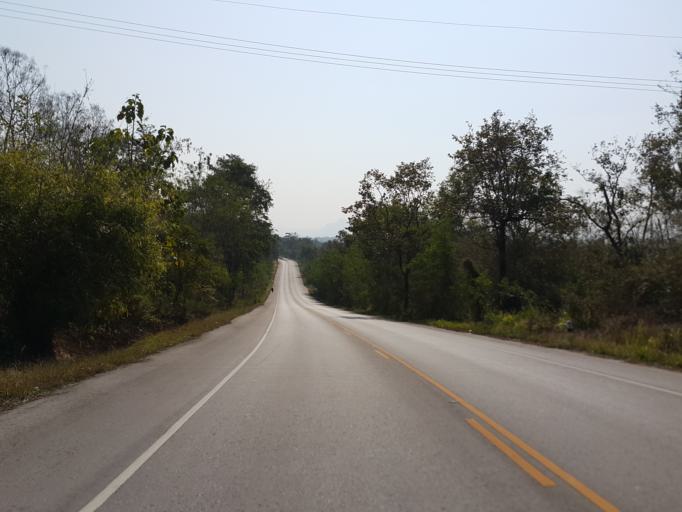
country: TH
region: Lampang
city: Mueang Pan
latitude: 18.8268
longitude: 99.5982
